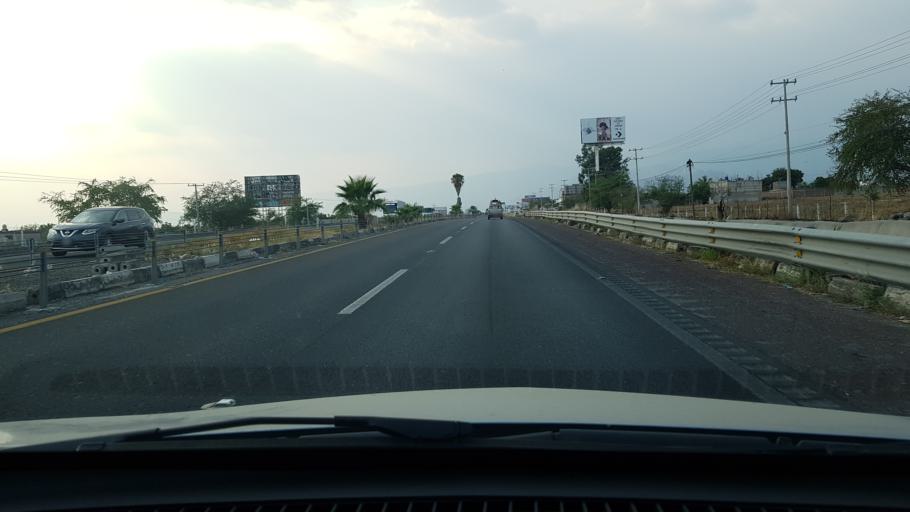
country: MX
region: Morelos
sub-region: Cuautla
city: Tierra Larga (Campo Nuevo)
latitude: 18.8593
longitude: -98.9444
